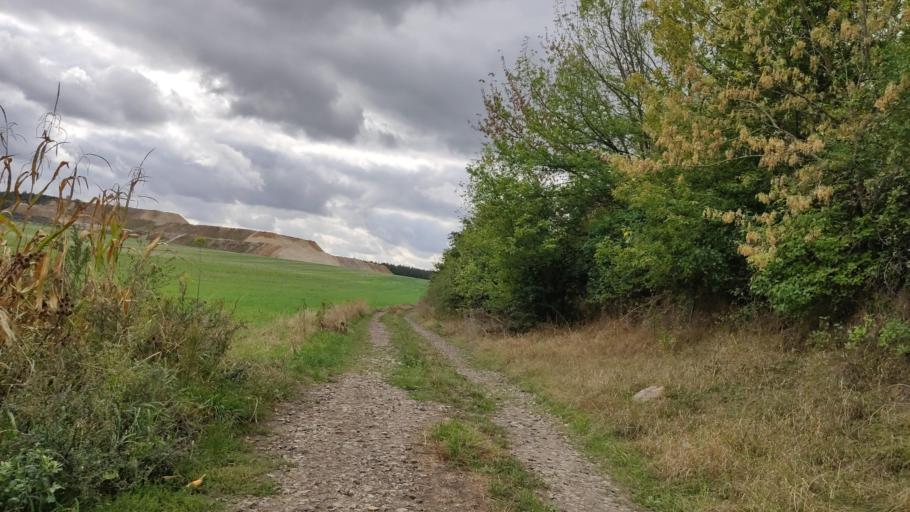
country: PL
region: Kujawsko-Pomorskie
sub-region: Powiat zninski
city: Barcin
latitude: 52.8418
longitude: 17.9526
